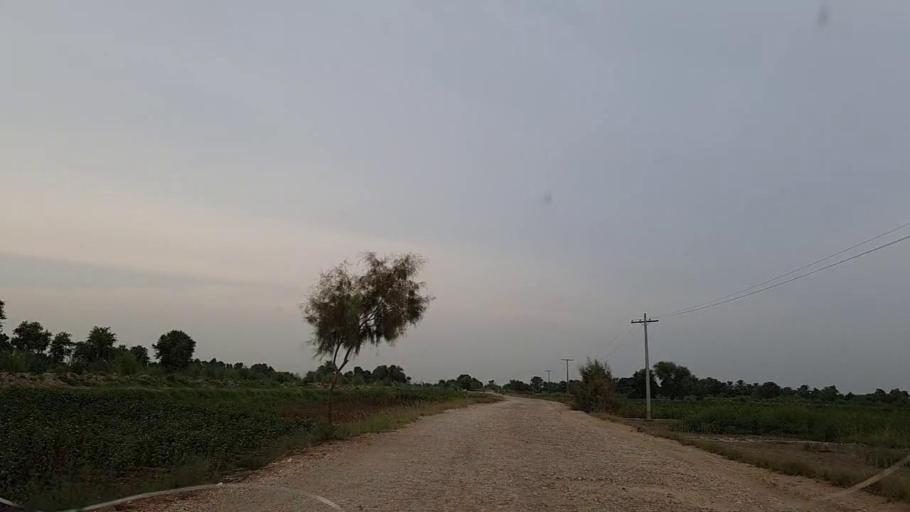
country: PK
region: Sindh
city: Mirpur Mathelo
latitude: 27.8658
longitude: 69.6328
